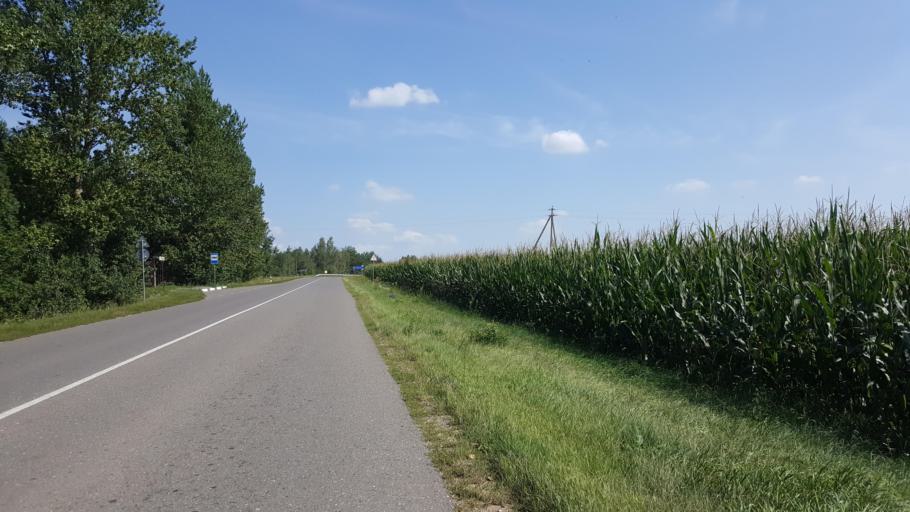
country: BY
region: Brest
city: Kamyanyuki
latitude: 52.4907
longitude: 23.6866
